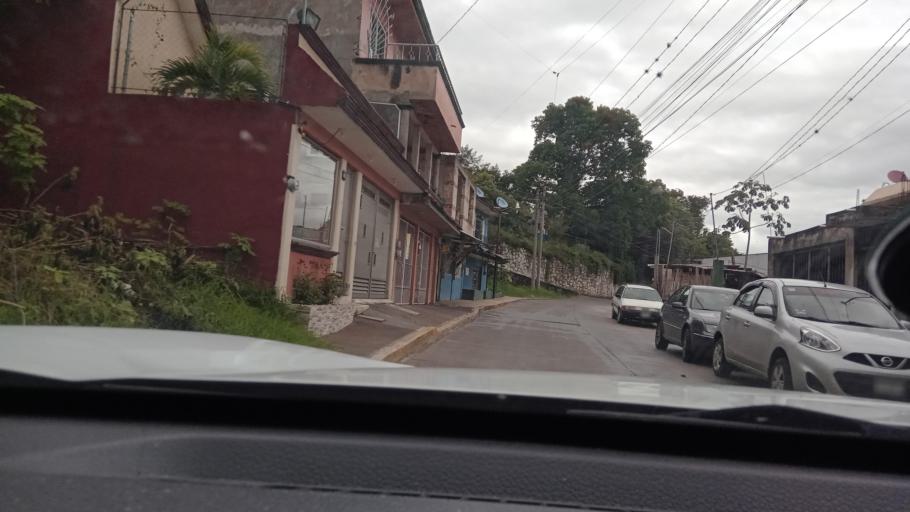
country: MX
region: Veracruz
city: Coatepec
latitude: 19.4459
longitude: -96.9602
